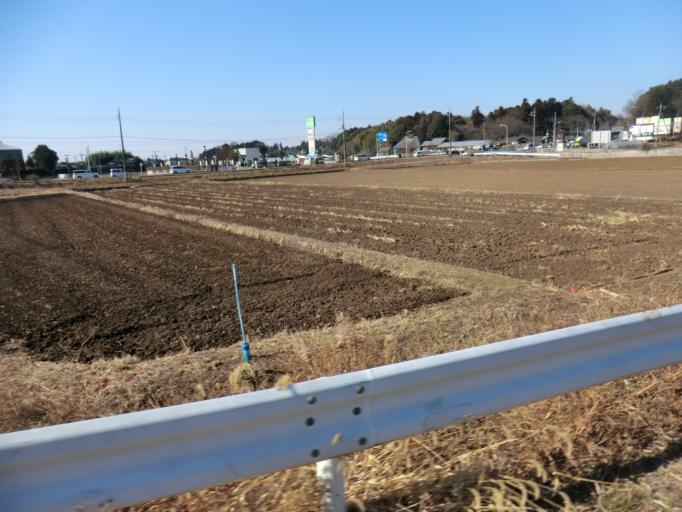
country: JP
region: Ibaraki
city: Naka
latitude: 36.0621
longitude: 140.0833
